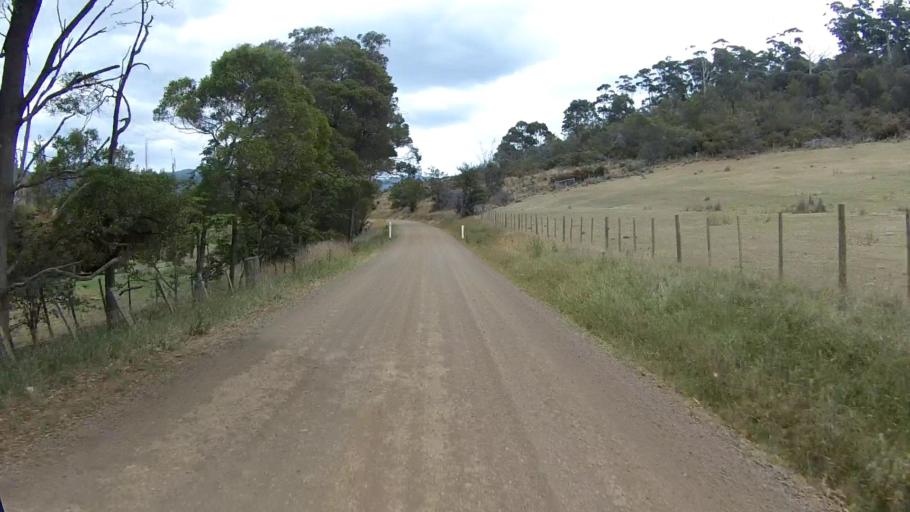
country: AU
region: Tasmania
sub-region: Sorell
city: Sorell
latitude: -42.6288
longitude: 147.9303
